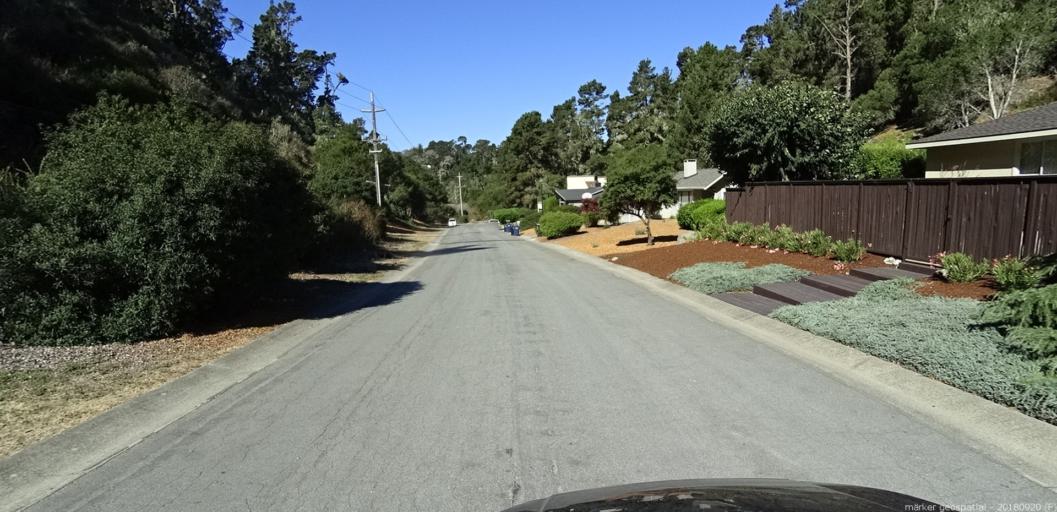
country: US
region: California
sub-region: Monterey County
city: Carmel-by-the-Sea
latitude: 36.5571
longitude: -121.9004
